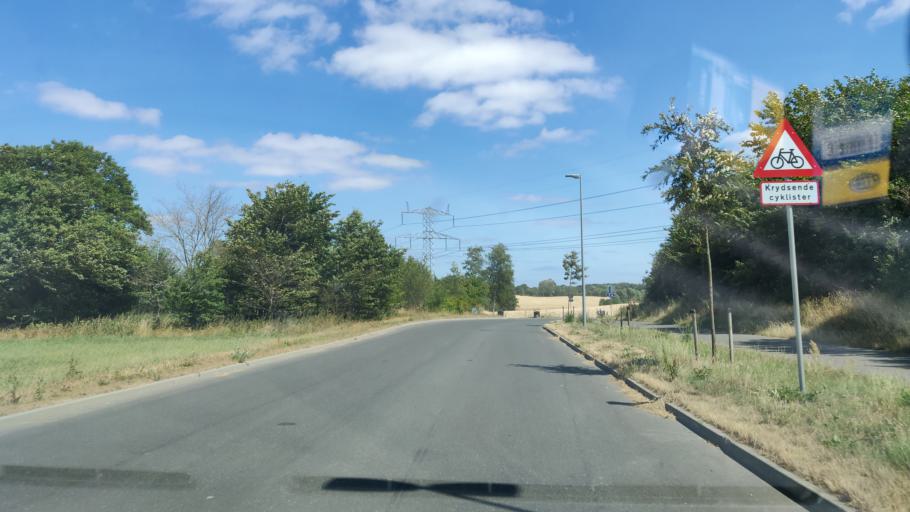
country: DK
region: South Denmark
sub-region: Kolding Kommune
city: Kolding
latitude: 55.5442
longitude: 9.5080
